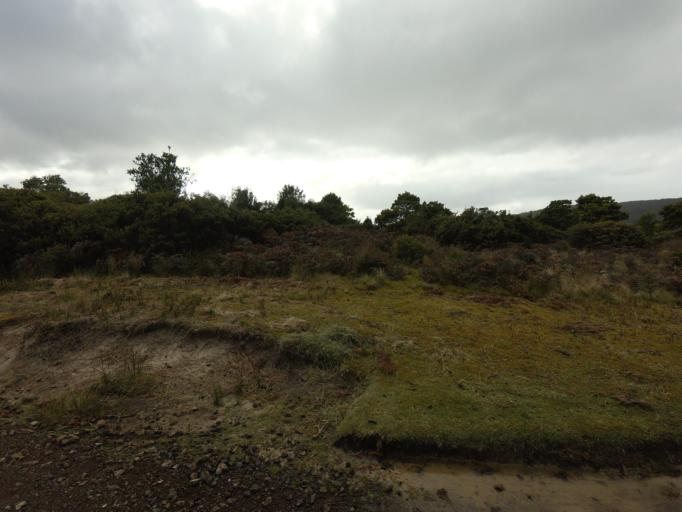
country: AU
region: Tasmania
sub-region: Huon Valley
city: Geeveston
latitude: -43.5790
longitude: 146.8871
